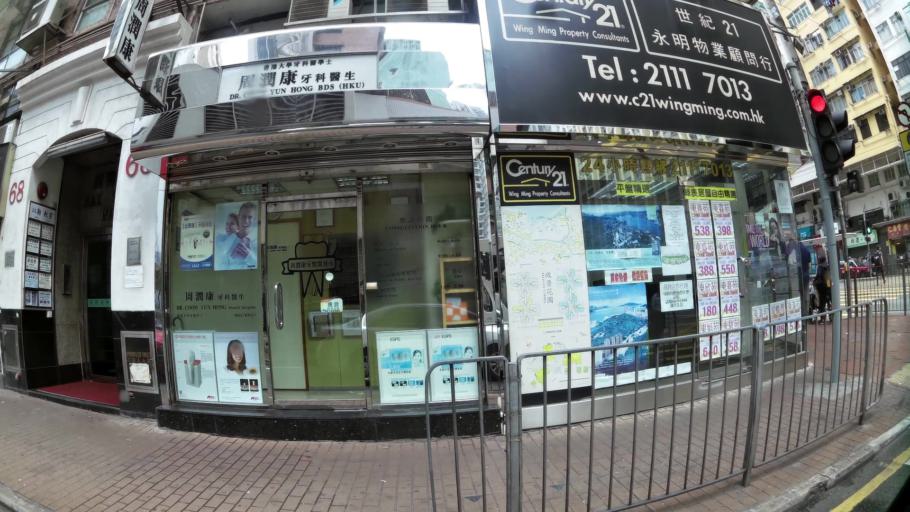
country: HK
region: Wanchai
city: Wan Chai
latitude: 22.2829
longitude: 114.2211
